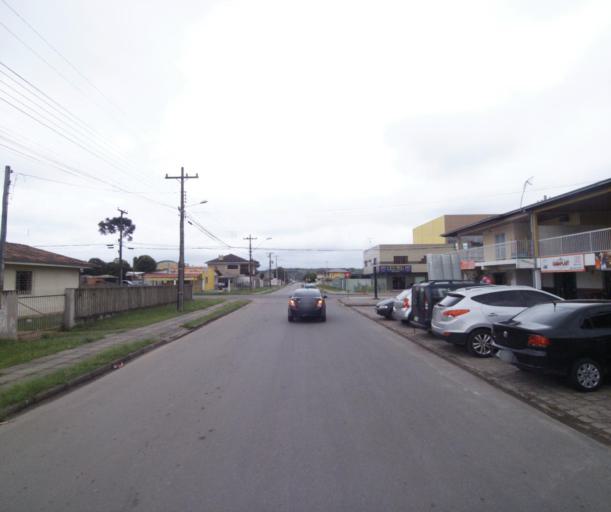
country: BR
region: Parana
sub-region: Quatro Barras
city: Quatro Barras
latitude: -25.3640
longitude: -49.0982
